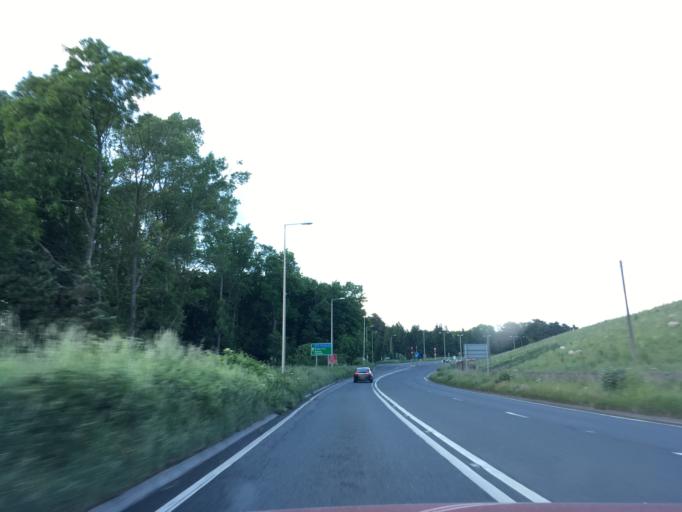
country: GB
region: England
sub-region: North Somerset
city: Winford
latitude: 51.4043
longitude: -2.6696
